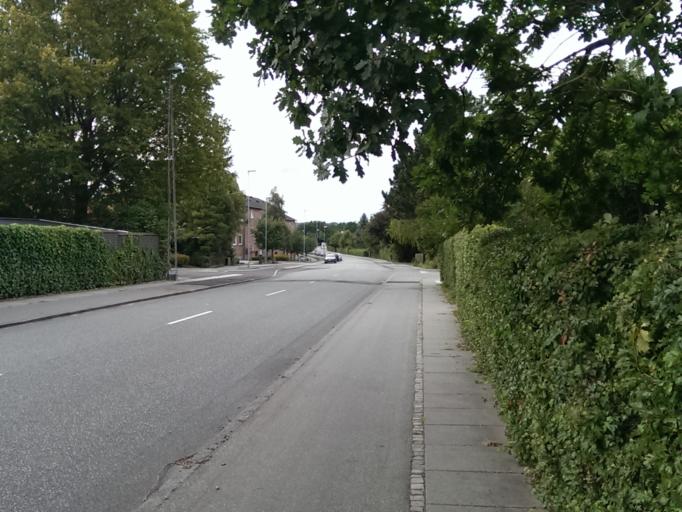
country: DK
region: Central Jutland
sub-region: Arhus Kommune
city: Arhus
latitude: 56.1349
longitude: 10.1792
